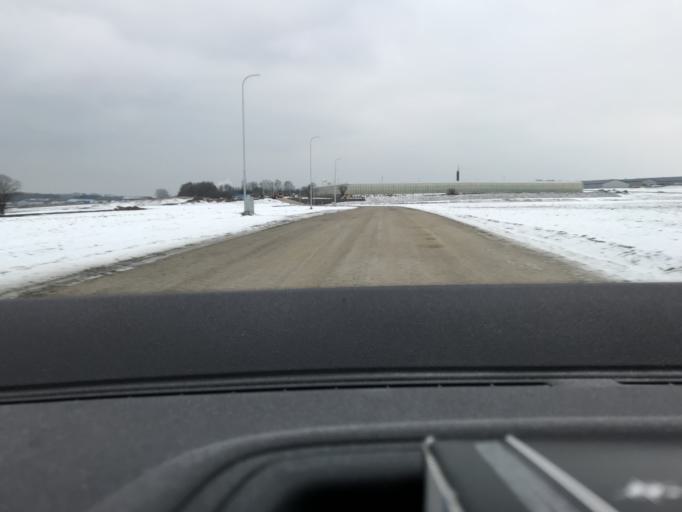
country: SE
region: Skane
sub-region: Ystads Kommun
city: Ystad
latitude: 55.4530
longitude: 13.8569
